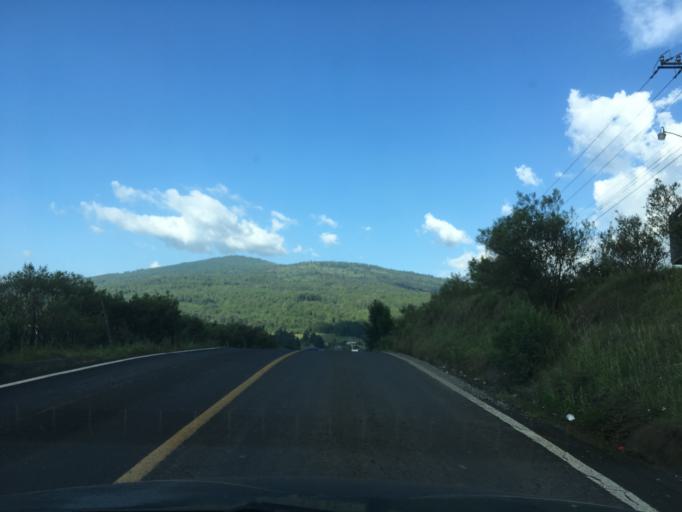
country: MX
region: Michoacan
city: Nahuatzen
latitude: 19.6466
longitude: -101.9163
